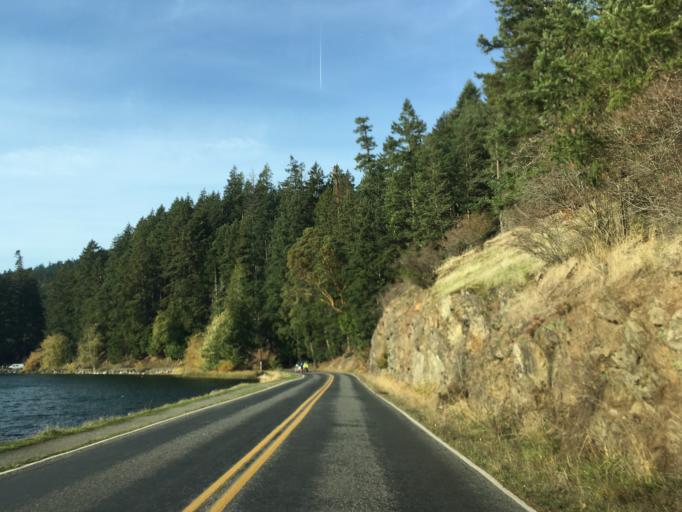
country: US
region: Washington
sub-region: San Juan County
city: Friday Harbor
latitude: 48.6533
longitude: -122.8520
